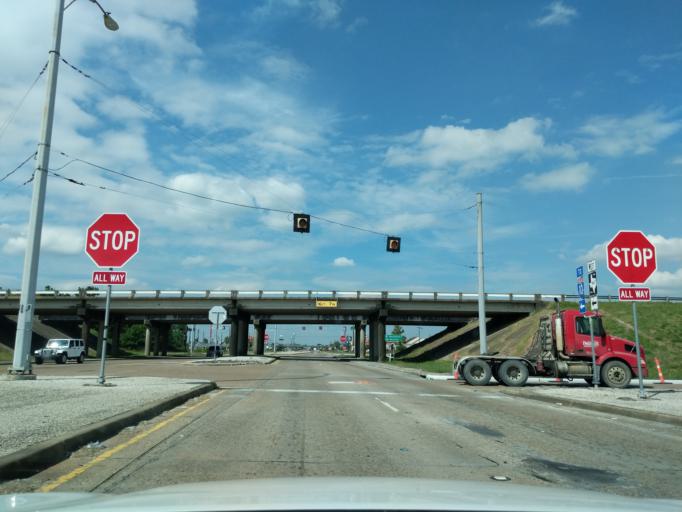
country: US
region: Texas
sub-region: Chambers County
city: Winnie
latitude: 29.8262
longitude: -94.3839
